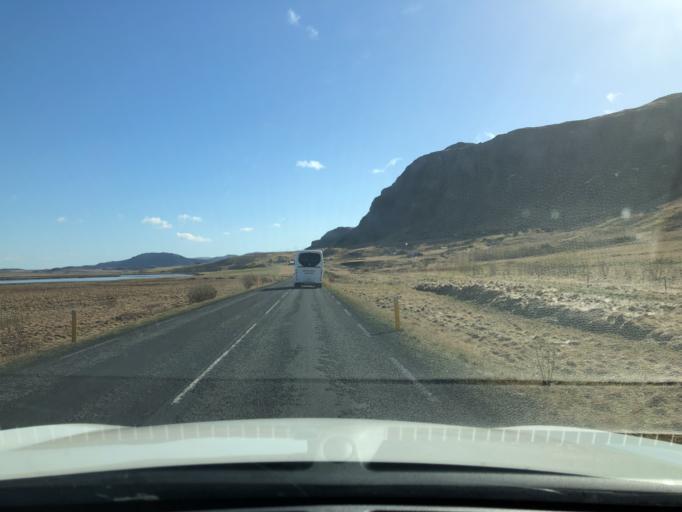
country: IS
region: West
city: Borgarnes
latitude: 64.5318
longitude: -21.7875
